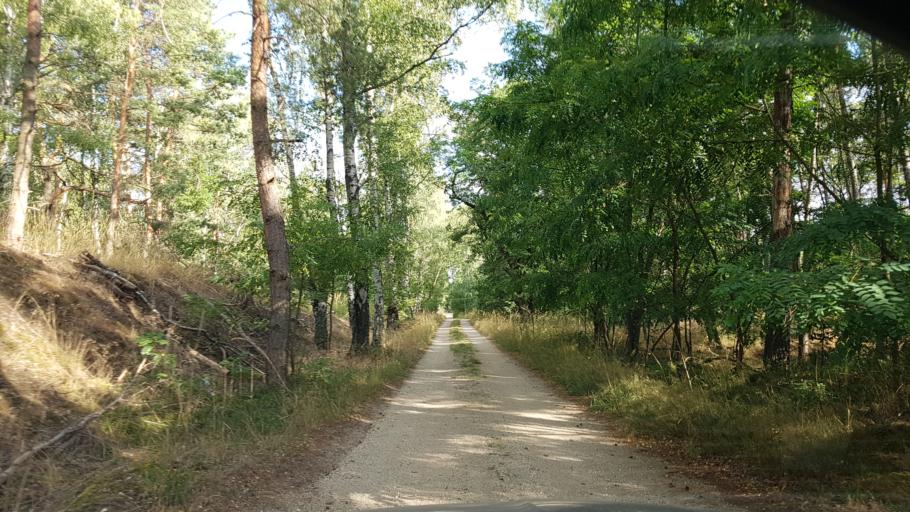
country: DE
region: Brandenburg
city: Trobitz
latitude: 51.6211
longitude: 13.4182
